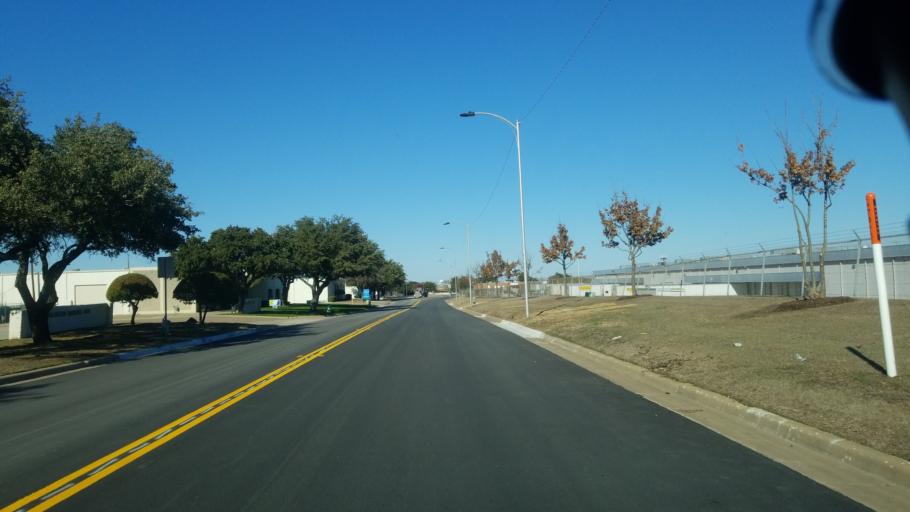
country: US
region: Texas
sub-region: Tarrant County
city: Arlington
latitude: 32.7524
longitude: -97.0542
